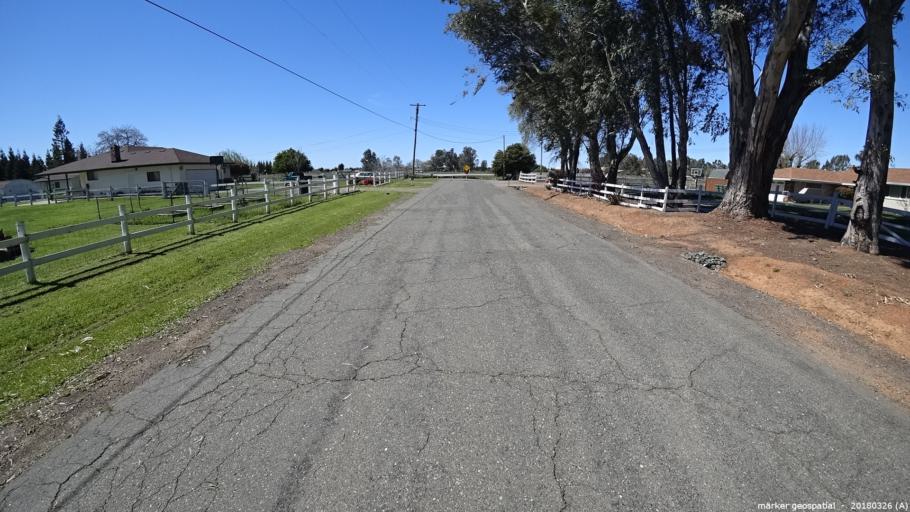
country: US
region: California
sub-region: Sacramento County
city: Wilton
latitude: 38.4570
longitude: -121.2922
